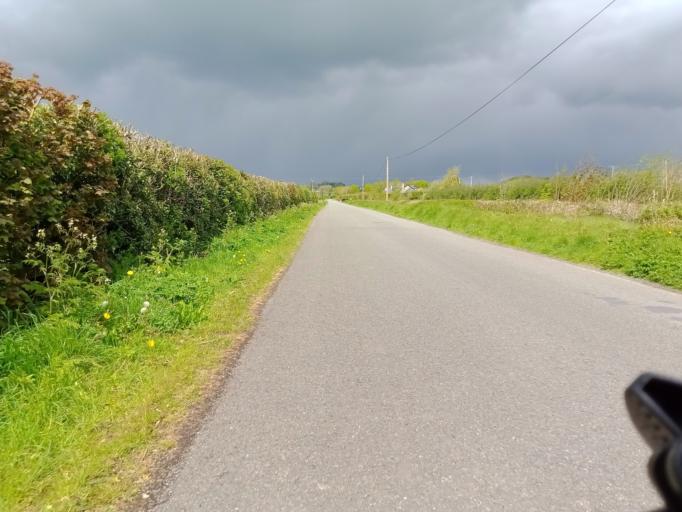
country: IE
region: Leinster
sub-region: Kilkenny
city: Kilkenny
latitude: 52.6788
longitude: -7.2642
